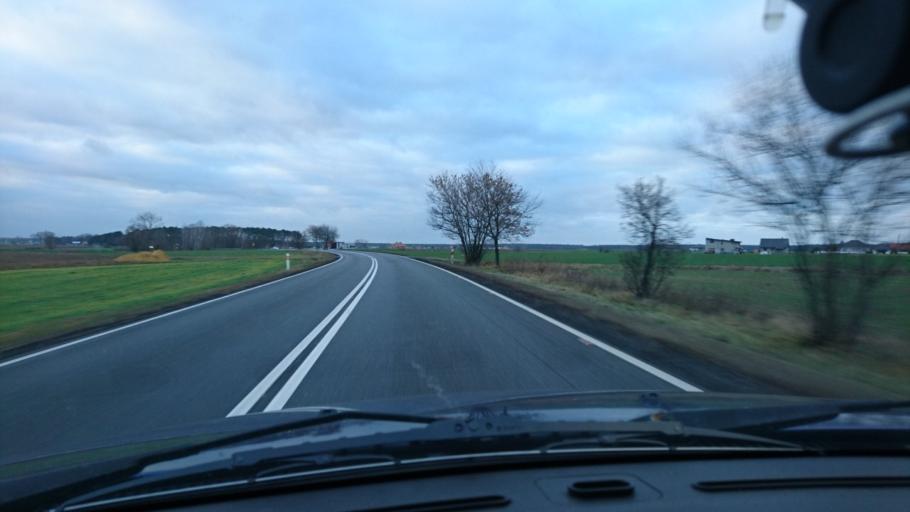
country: PL
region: Greater Poland Voivodeship
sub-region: Powiat kepinski
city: Opatow
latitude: 51.2194
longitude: 18.1371
